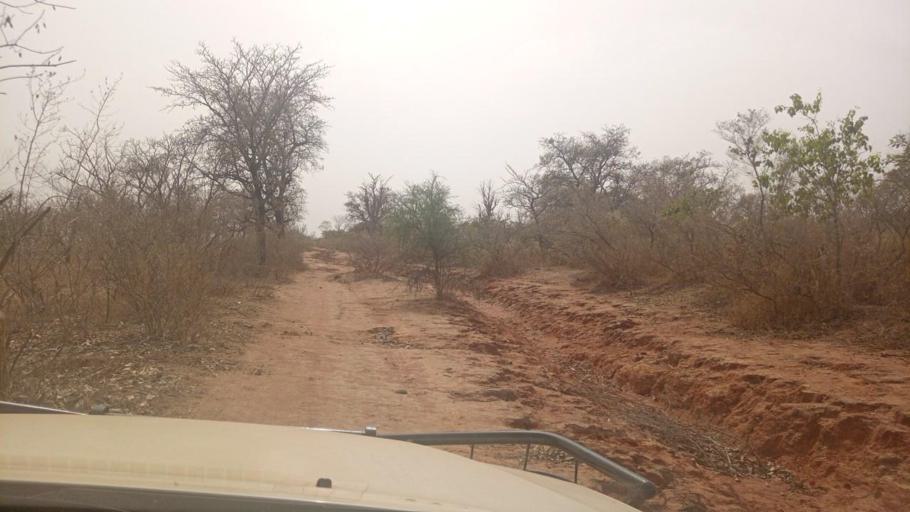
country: BF
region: Boucle du Mouhoun
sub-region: Province des Banwa
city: Salanso
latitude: 12.1568
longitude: -4.2458
